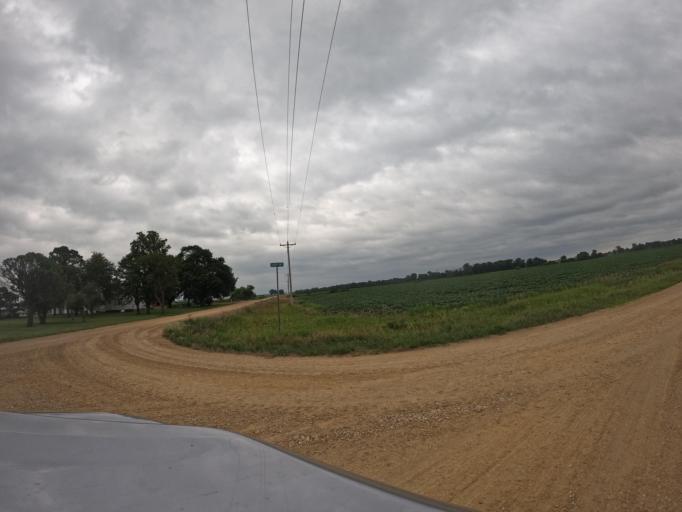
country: US
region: Iowa
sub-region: Clinton County
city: De Witt
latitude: 41.7862
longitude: -90.4369
